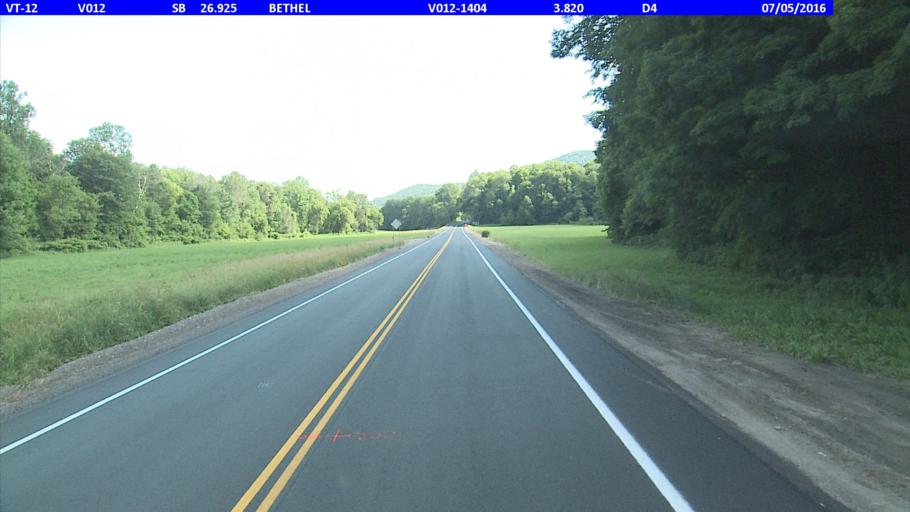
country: US
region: Vermont
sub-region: Orange County
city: Randolph
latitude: 43.8528
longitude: -72.6470
